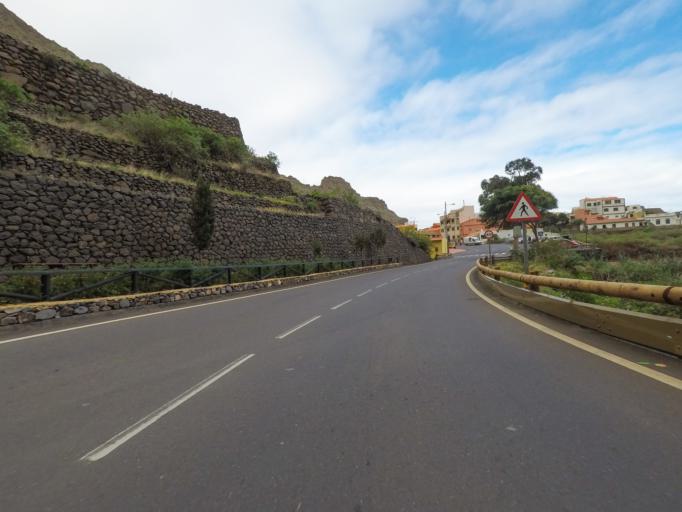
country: ES
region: Canary Islands
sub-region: Provincia de Santa Cruz de Tenerife
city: Agulo
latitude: 28.1850
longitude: -17.1944
